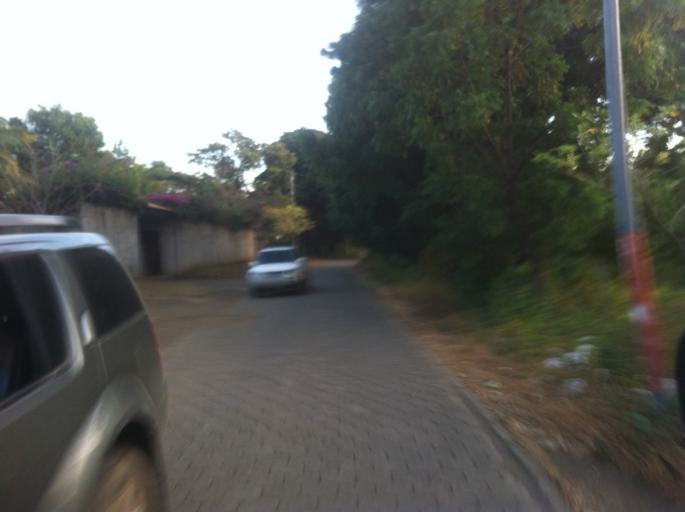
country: NI
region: Managua
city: Ciudad Sandino
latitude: 12.0944
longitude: -86.3342
